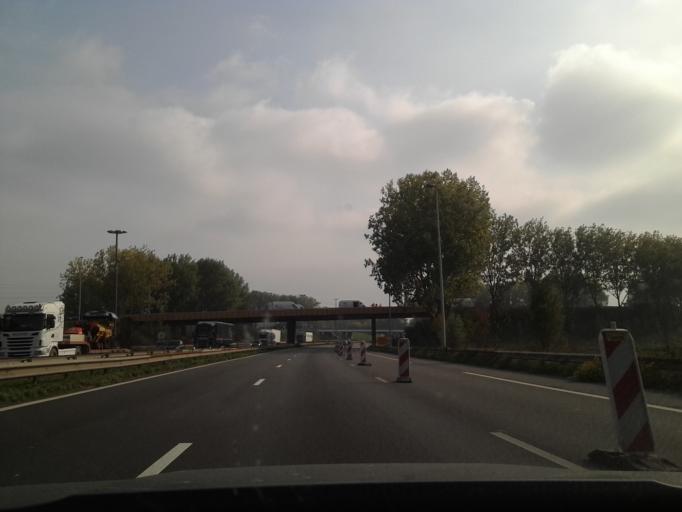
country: FR
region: Nord-Pas-de-Calais
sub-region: Departement du Nord
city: Lezennes
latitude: 50.6011
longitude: 3.1267
